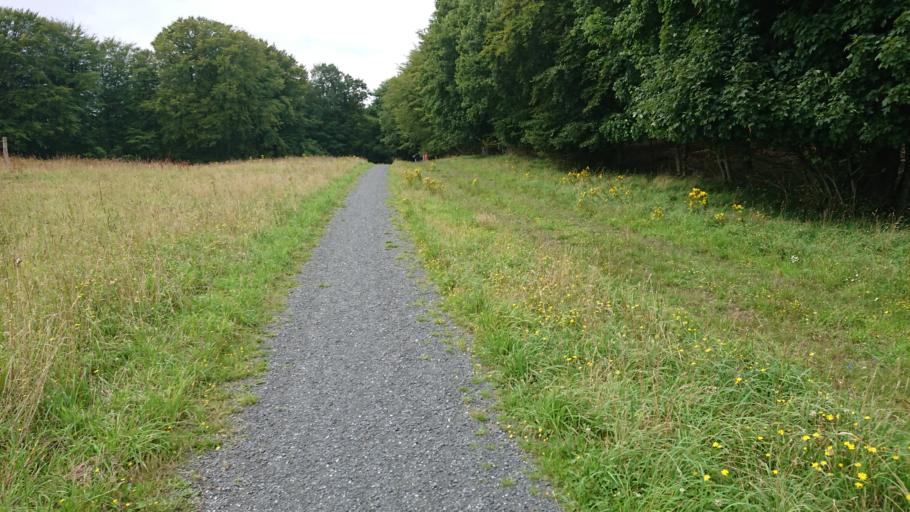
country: DK
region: North Denmark
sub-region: Hjorring Kommune
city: Sindal
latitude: 57.4804
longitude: 10.1779
